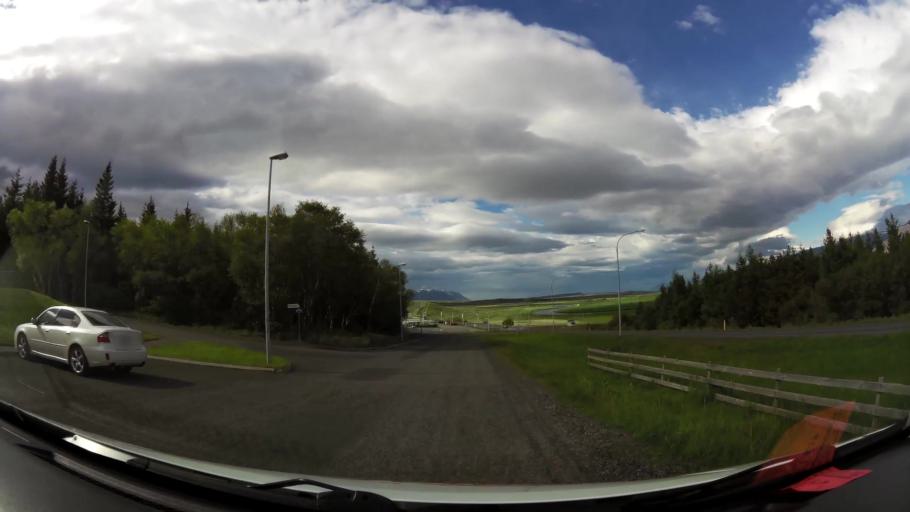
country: IS
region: Northwest
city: Saudarkrokur
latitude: 65.5515
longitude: -19.4441
